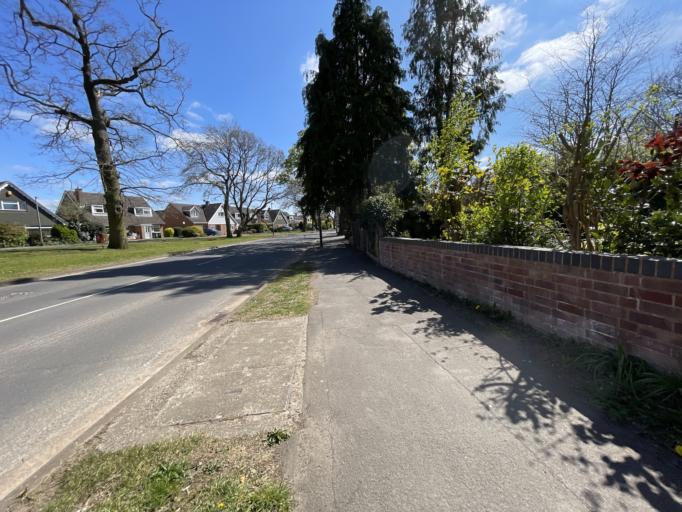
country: GB
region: England
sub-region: Warwickshire
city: Dunchurch
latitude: 52.3501
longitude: -1.2888
